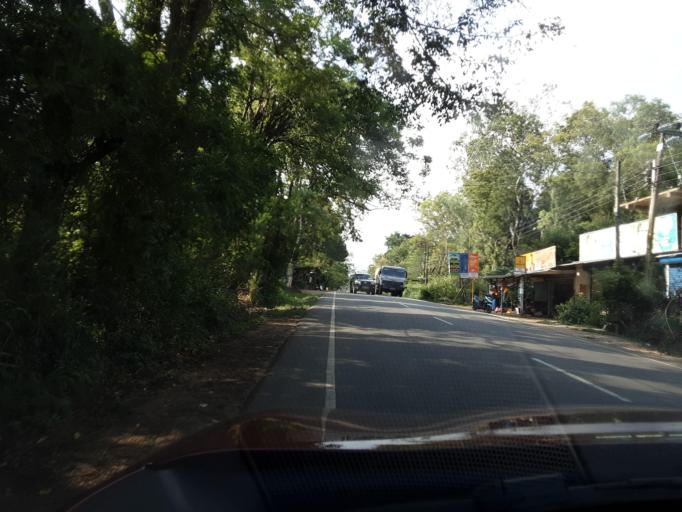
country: LK
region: Uva
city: Haputale
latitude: 6.6657
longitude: 81.1136
